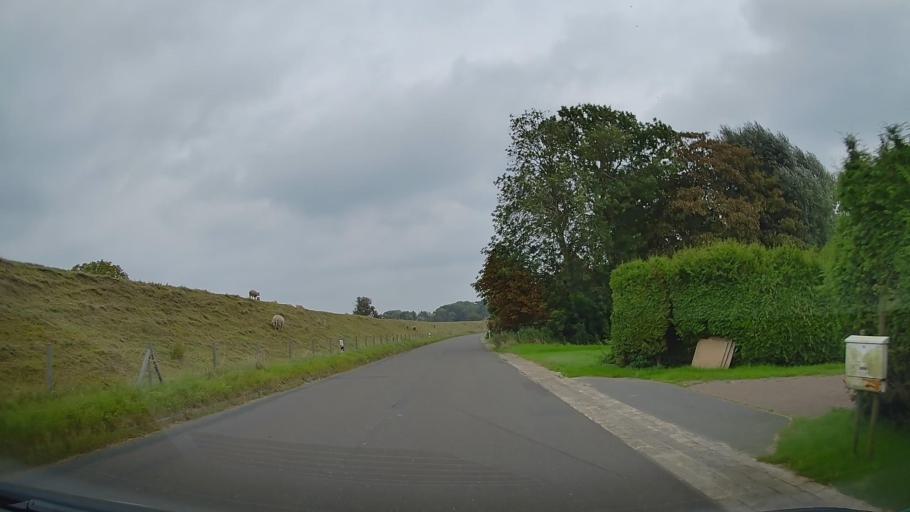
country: DE
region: Lower Saxony
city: Geversdorf
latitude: 53.8245
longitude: 9.0748
